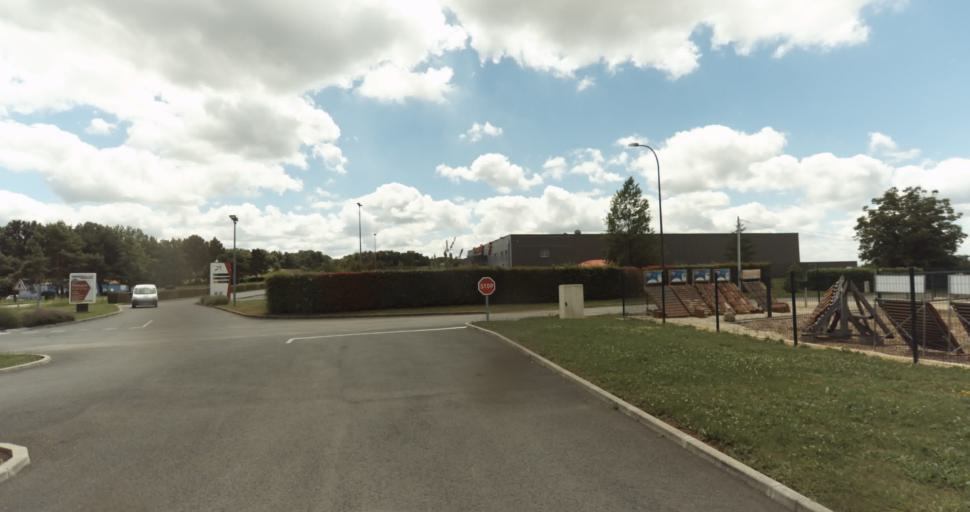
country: FR
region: Aquitaine
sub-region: Departement de la Dordogne
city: Beaumont-du-Perigord
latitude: 44.7545
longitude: 0.7727
